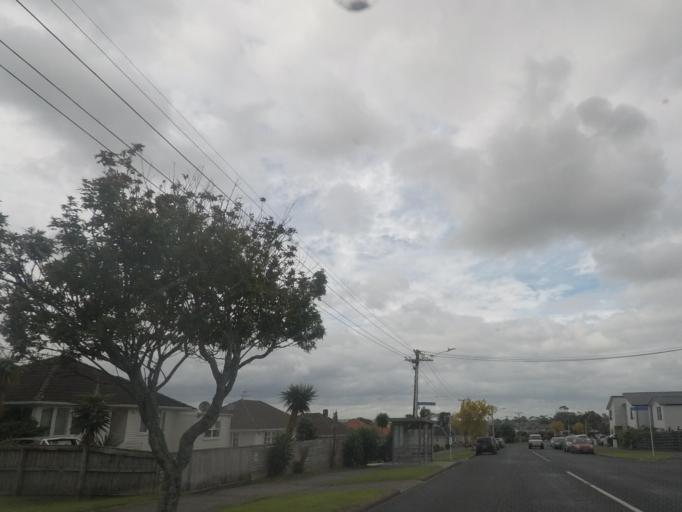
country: NZ
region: Auckland
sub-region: Auckland
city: Tamaki
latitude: -36.8740
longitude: 174.8740
